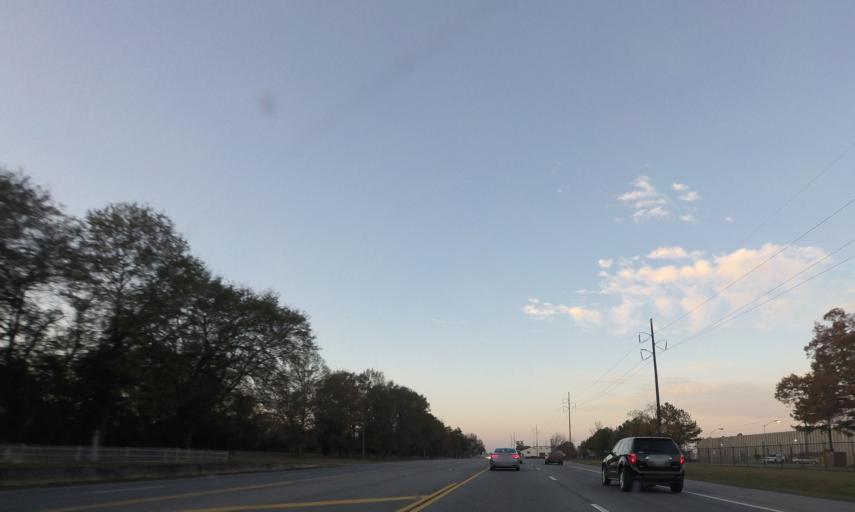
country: US
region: Georgia
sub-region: Houston County
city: Robins Air Force Base
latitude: 32.6013
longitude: -83.5934
